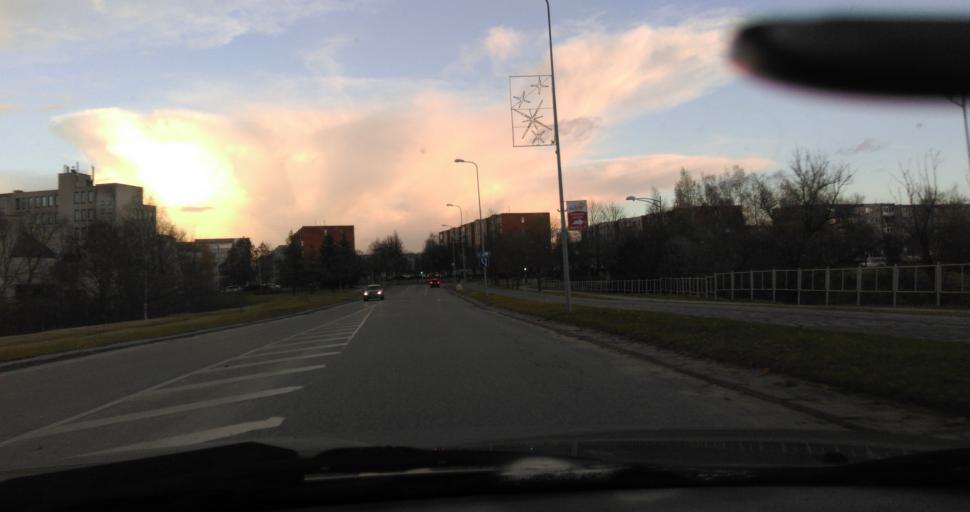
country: LT
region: Utenos apskritis
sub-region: Utena
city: Utena
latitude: 55.5100
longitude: 25.5954
